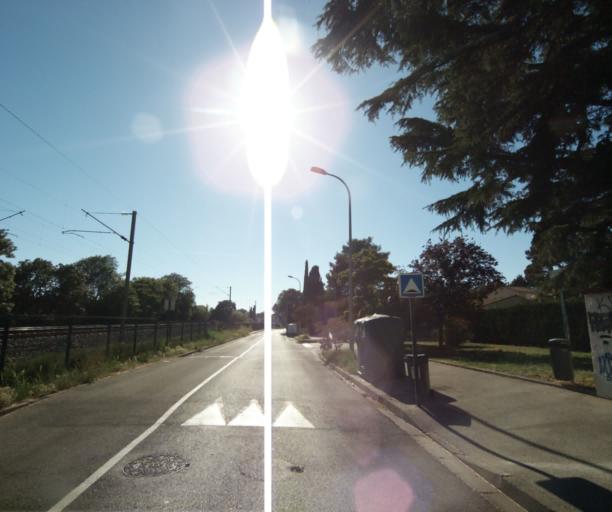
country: FR
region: Provence-Alpes-Cote d'Azur
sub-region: Departement du Var
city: La Garde
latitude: 43.1139
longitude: 5.9916
